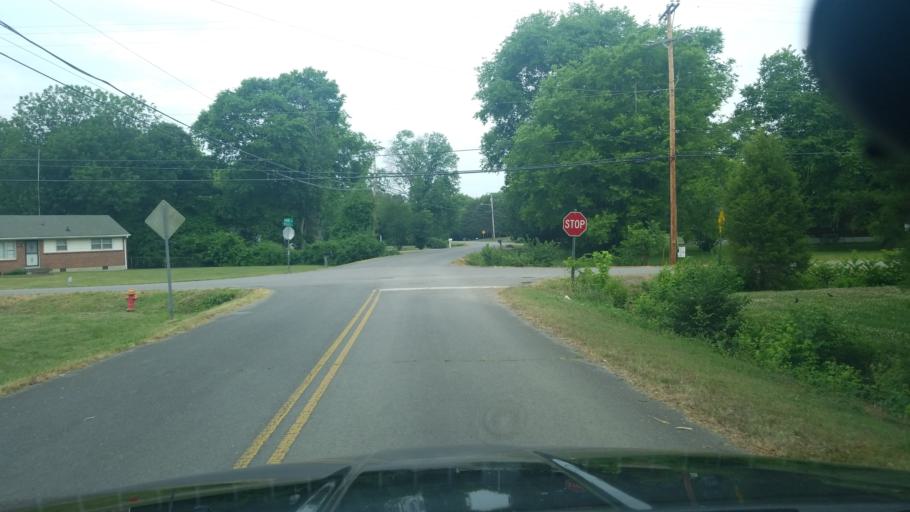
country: US
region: Tennessee
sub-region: Davidson County
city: Goodlettsville
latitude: 36.2635
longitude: -86.7392
